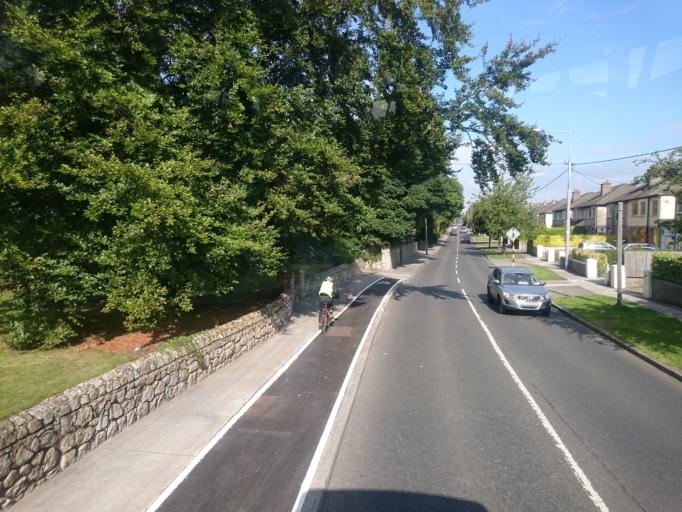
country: IE
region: Leinster
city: Sandyford
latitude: 53.2872
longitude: -6.2282
